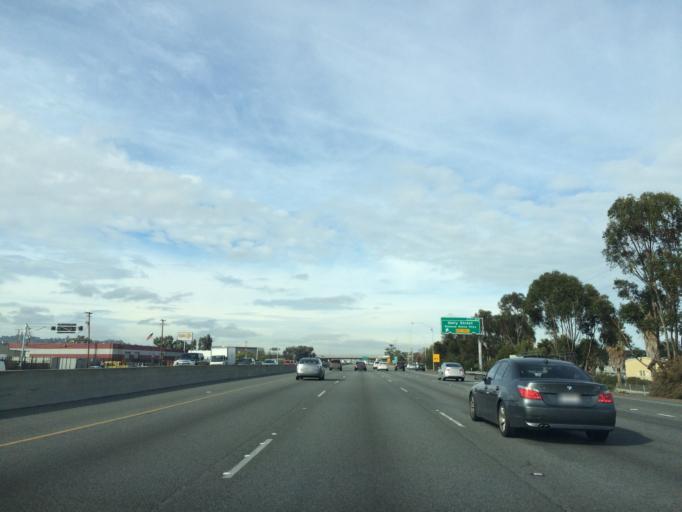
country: US
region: California
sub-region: San Mateo County
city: San Carlos
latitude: 37.5099
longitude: -122.2514
